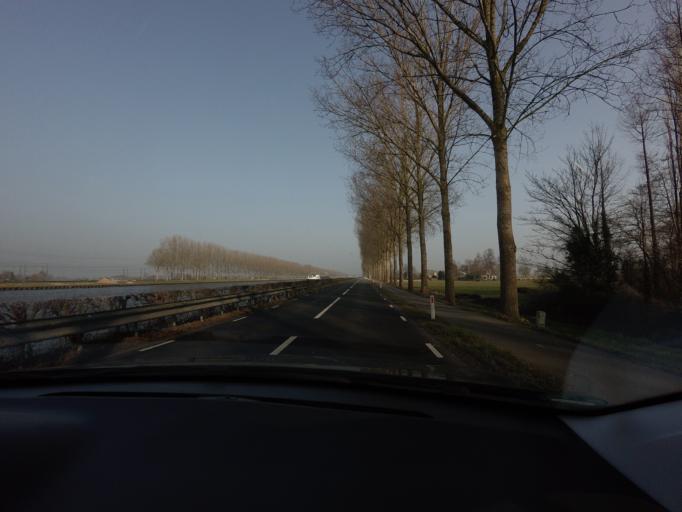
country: NL
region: Utrecht
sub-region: Stichtse Vecht
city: Vreeland
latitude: 52.2280
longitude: 5.0080
